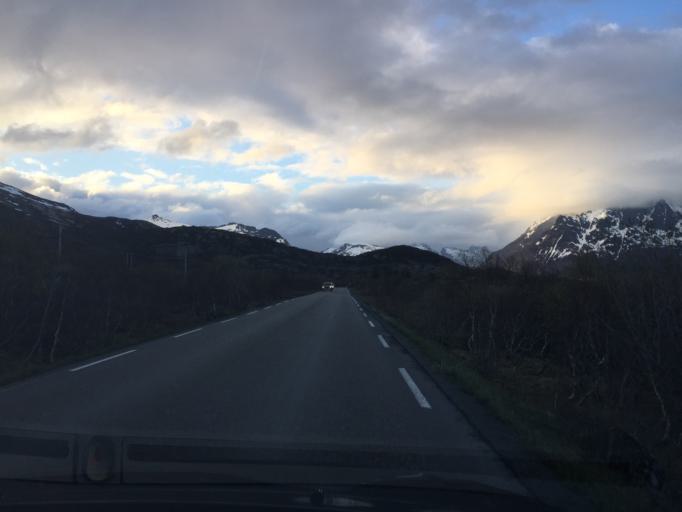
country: NO
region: Nordland
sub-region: Vagan
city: Svolvaer
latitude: 68.2912
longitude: 14.6972
